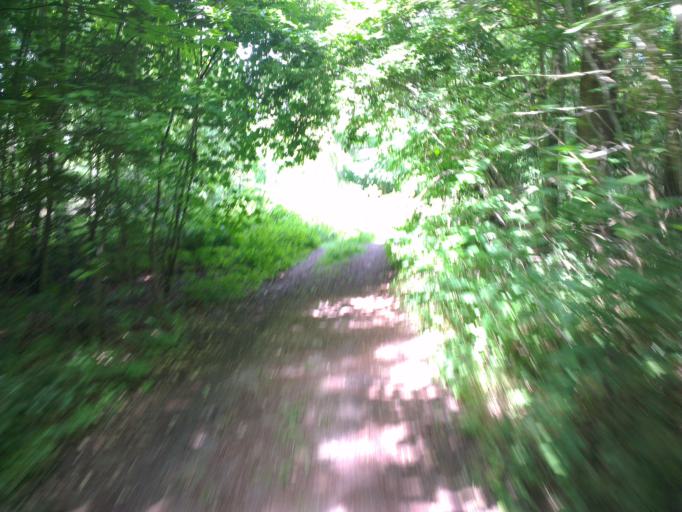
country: DK
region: Capital Region
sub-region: Frederikssund Kommune
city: Jaegerspris
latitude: 55.8151
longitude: 11.9328
